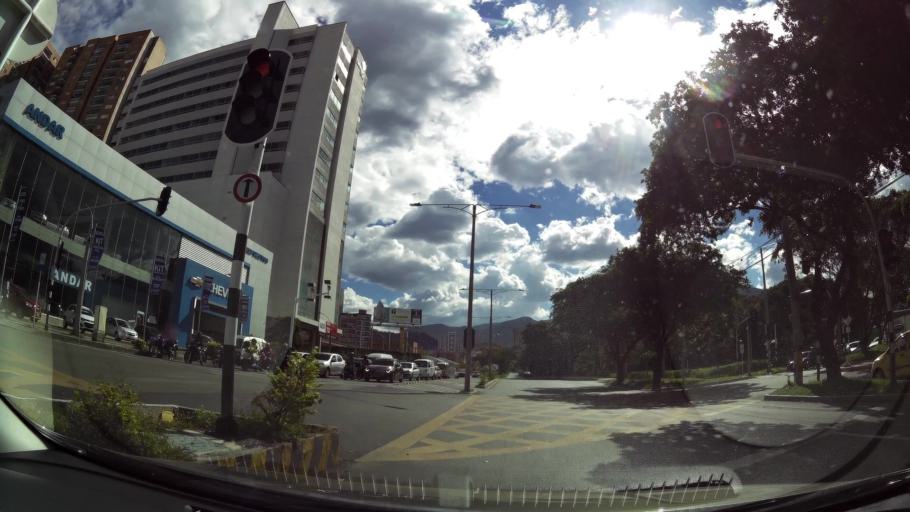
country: CO
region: Antioquia
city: Sabaneta
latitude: 6.1578
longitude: -75.6095
